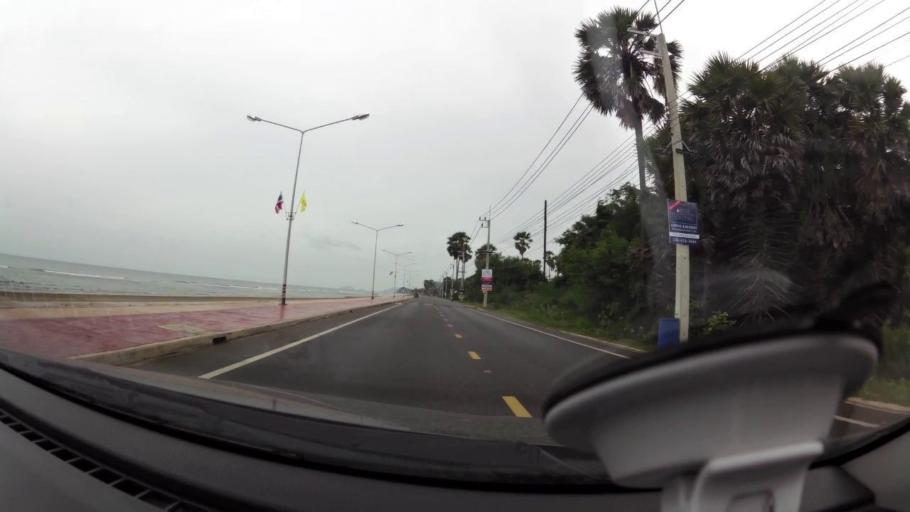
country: TH
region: Prachuap Khiri Khan
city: Pran Buri
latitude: 12.3758
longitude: 100.0002
